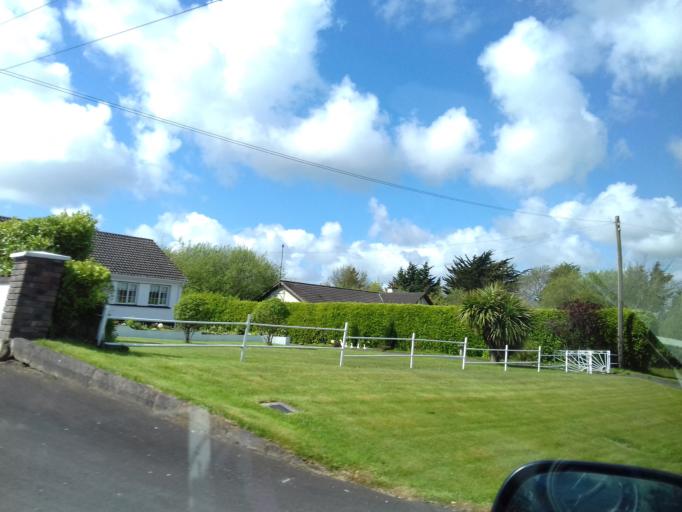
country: IE
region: Leinster
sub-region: Loch Garman
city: Castlebridge
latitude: 52.3689
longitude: -6.4458
